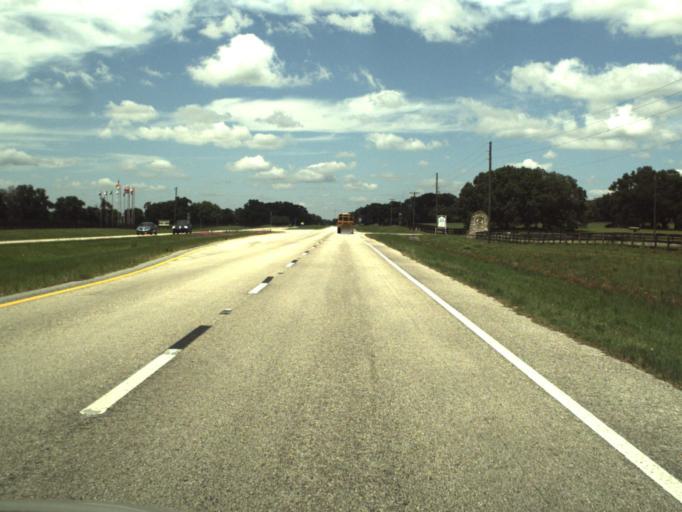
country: US
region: Florida
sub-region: Marion County
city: Citra
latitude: 29.3875
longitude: -82.1876
